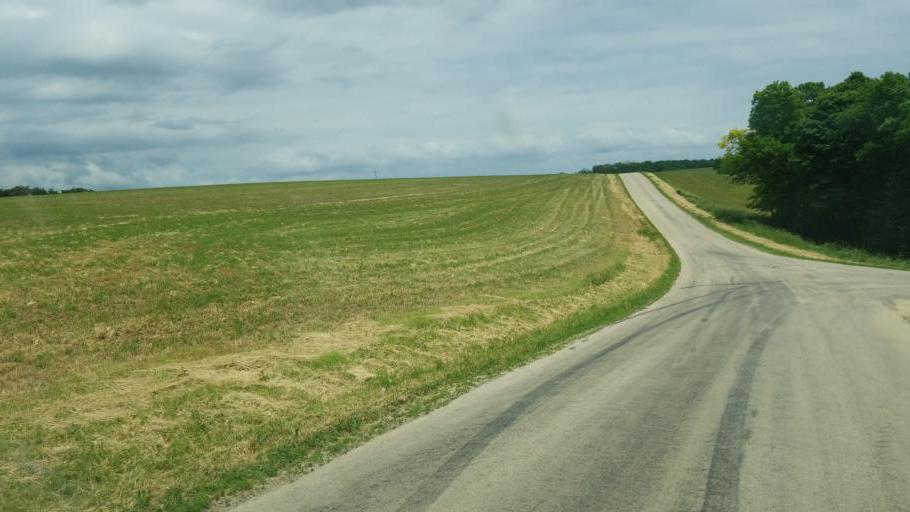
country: US
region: Wisconsin
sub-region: Monroe County
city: Cashton
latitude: 43.7008
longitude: -90.6300
